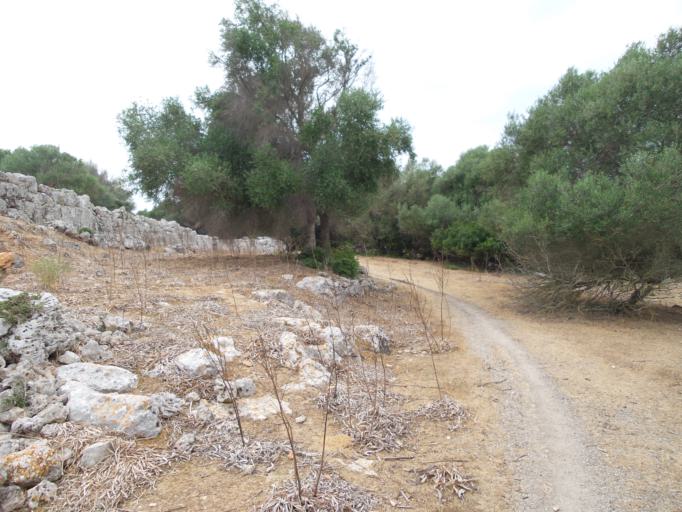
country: ES
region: Balearic Islands
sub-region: Illes Balears
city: Ciutadella
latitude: 39.9543
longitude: 3.8763
